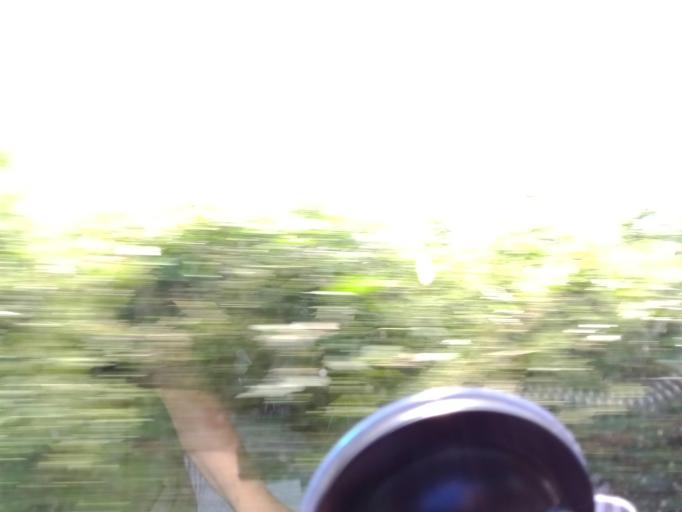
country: IE
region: Leinster
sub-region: Kilkenny
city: Thomastown
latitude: 52.5555
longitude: -7.1034
